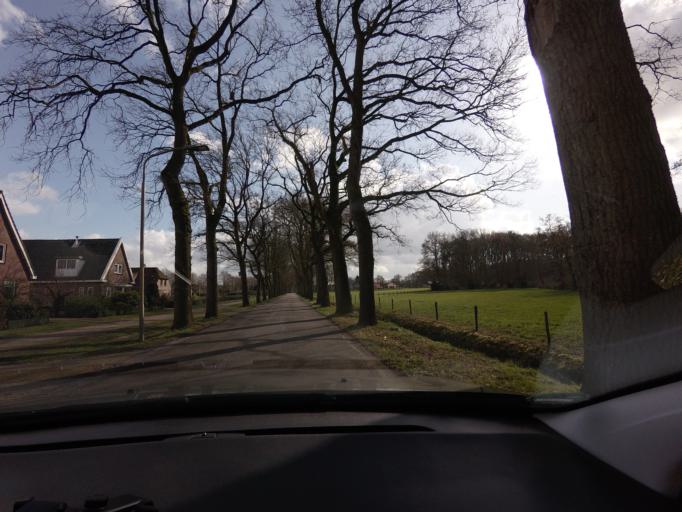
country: NL
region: Drenthe
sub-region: Gemeente Assen
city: Assen
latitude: 52.8553
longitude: 6.5968
